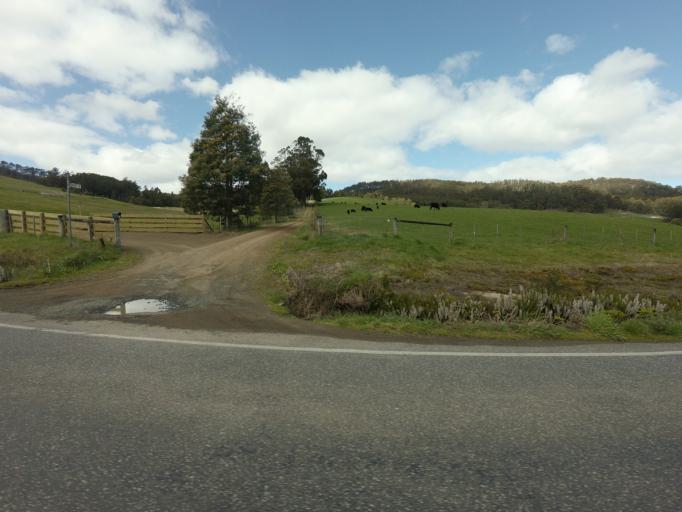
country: AU
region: Tasmania
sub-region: Huon Valley
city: Cygnet
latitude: -43.2882
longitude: 147.0107
